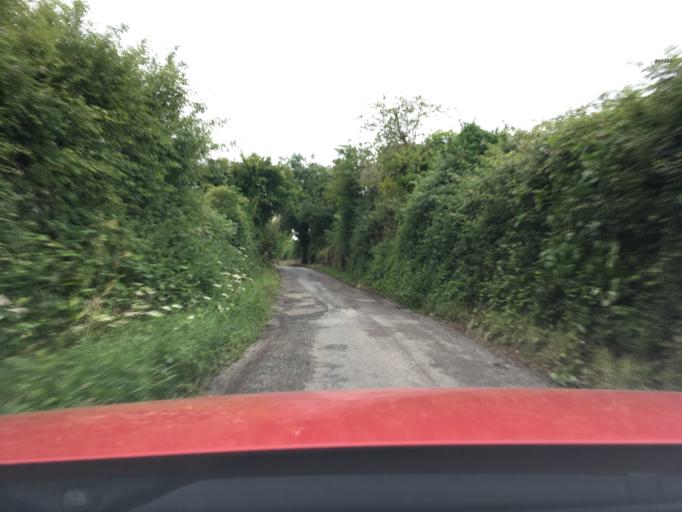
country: GB
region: England
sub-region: Gloucestershire
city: Stonehouse
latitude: 51.7858
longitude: -2.3851
